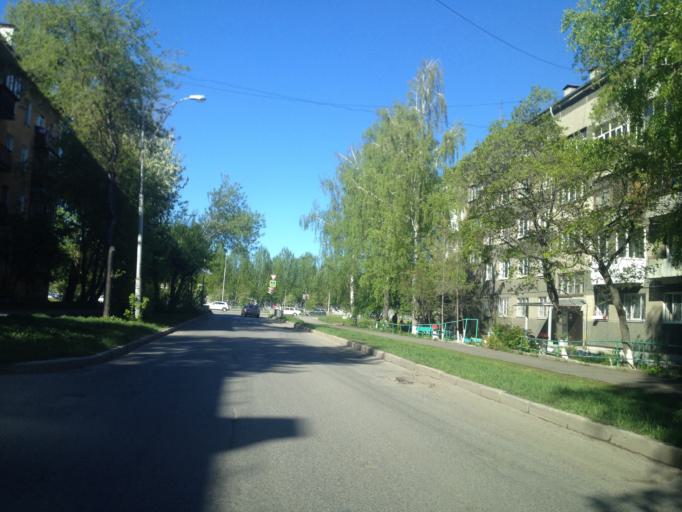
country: RU
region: Sverdlovsk
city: Shuvakish
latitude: 56.8718
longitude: 60.5306
